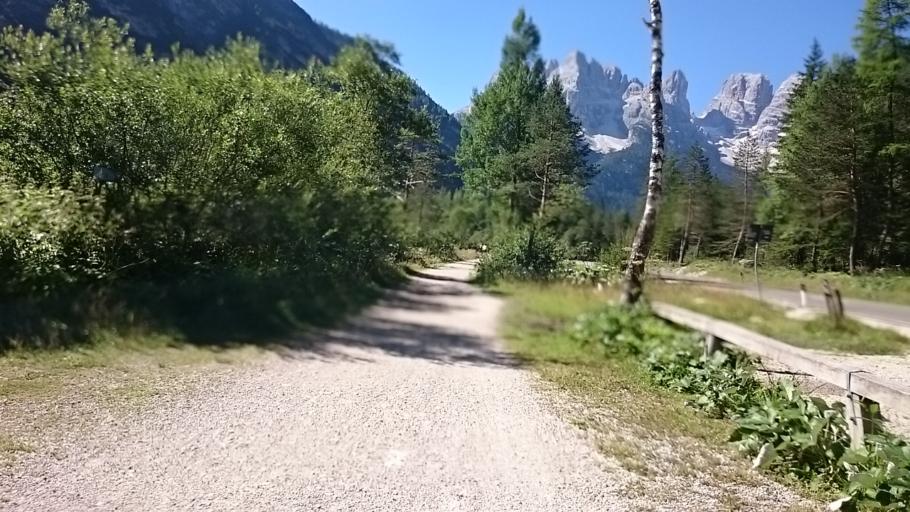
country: IT
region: Trentino-Alto Adige
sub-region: Bolzano
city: Dobbiaco
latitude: 46.6300
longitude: 12.2290
